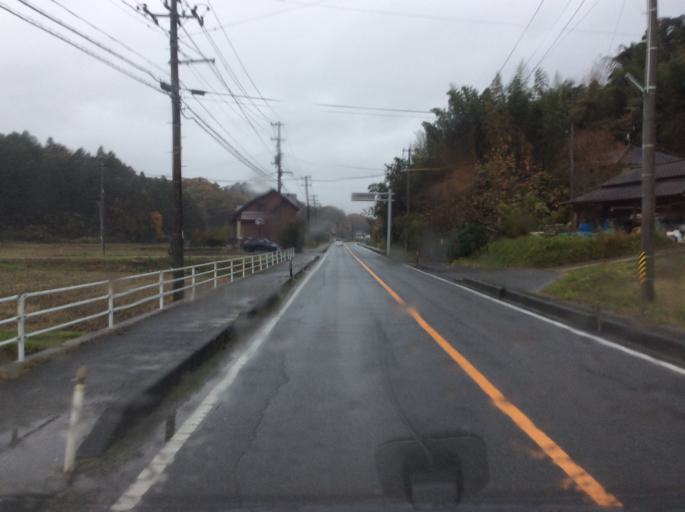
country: JP
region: Fukushima
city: Iwaki
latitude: 37.1142
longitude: 140.9756
